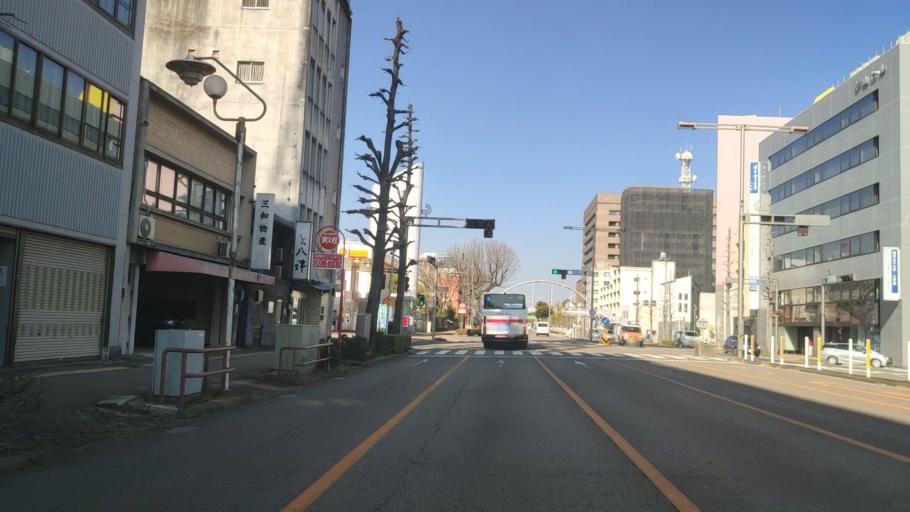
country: JP
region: Gifu
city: Gifu-shi
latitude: 35.4219
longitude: 136.7578
